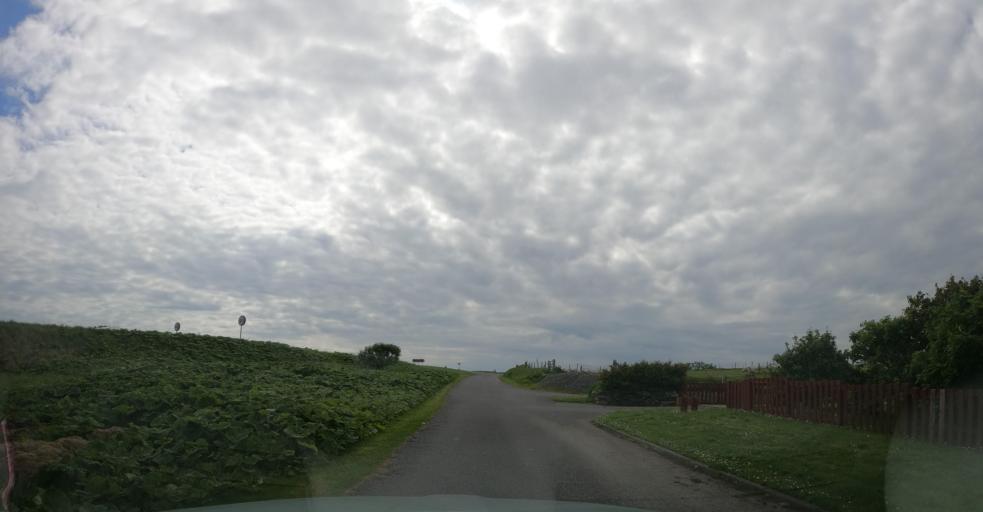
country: GB
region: Scotland
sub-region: Eilean Siar
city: Isle of Lewis
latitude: 58.2867
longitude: -6.2841
